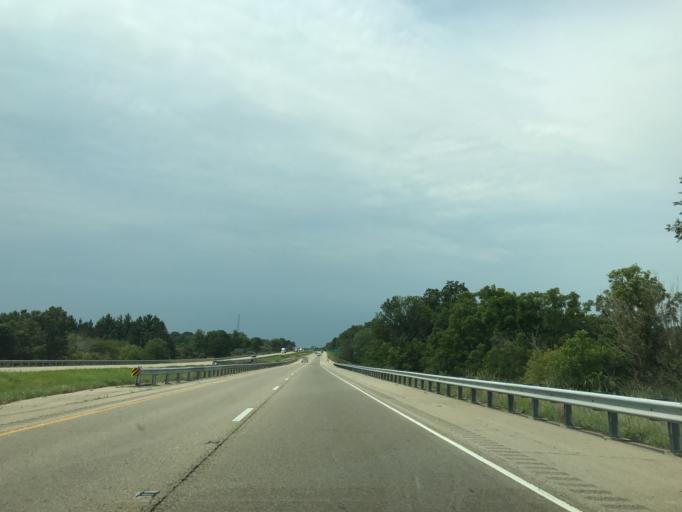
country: US
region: Illinois
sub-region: Bureau County
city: Depue
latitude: 41.3998
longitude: -89.3578
